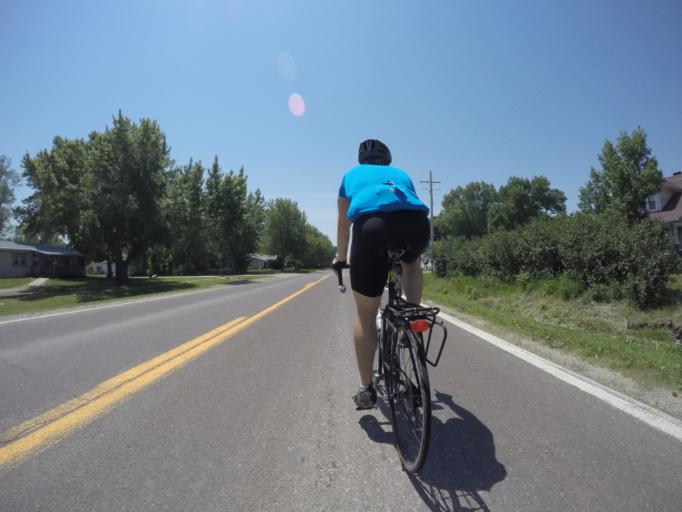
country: US
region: Nebraska
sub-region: Pawnee County
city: Pawnee City
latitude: 40.0373
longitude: -96.0482
